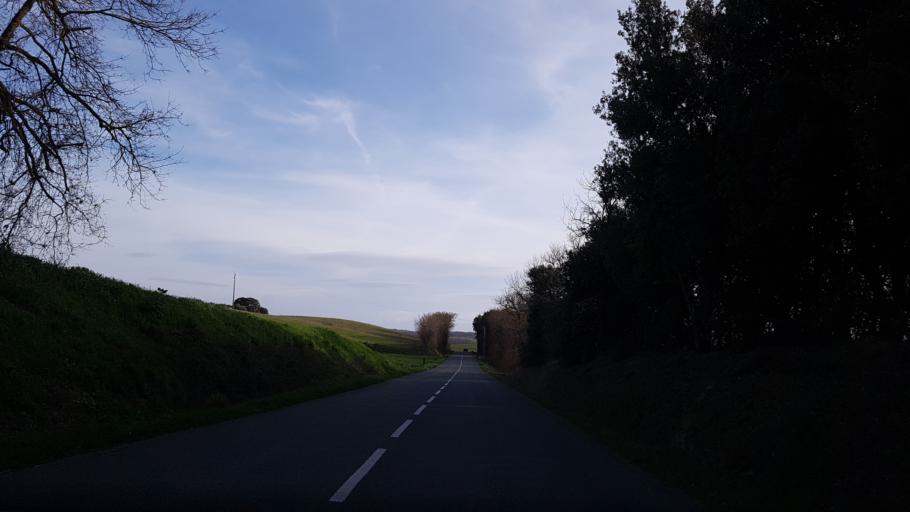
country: FR
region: Languedoc-Roussillon
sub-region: Departement de l'Aude
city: Villeneuve-la-Comptal
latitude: 43.2308
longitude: 1.9201
